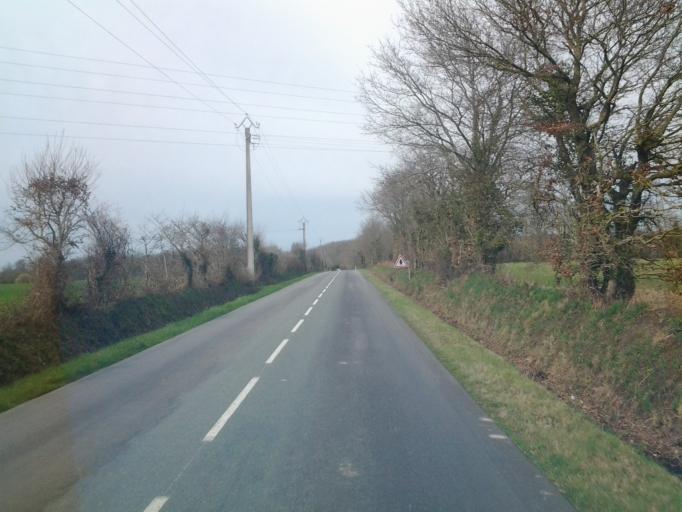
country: FR
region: Pays de la Loire
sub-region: Departement de la Vendee
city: Venansault
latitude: 46.6712
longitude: -1.4757
